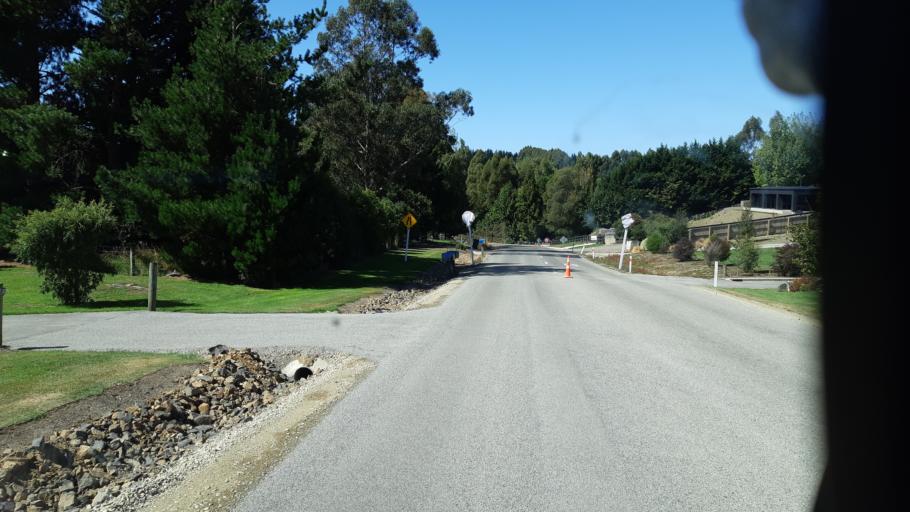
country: NZ
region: Otago
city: Oamaru
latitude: -45.0800
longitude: 170.9281
